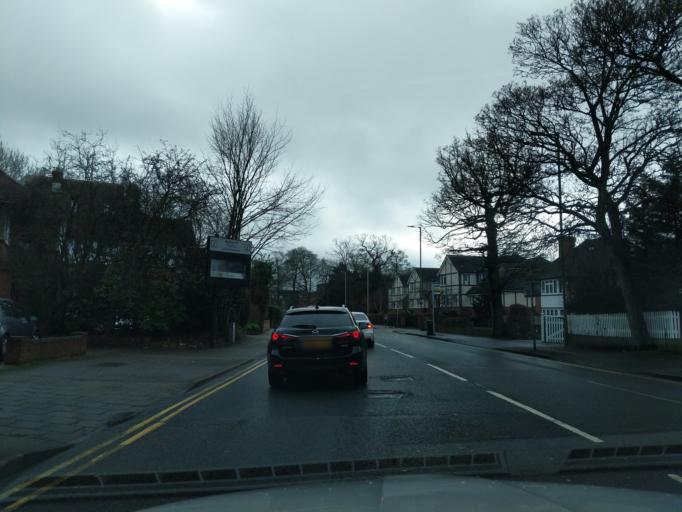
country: GB
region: England
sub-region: Hertfordshire
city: Watford
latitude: 51.6626
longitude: -0.4080
